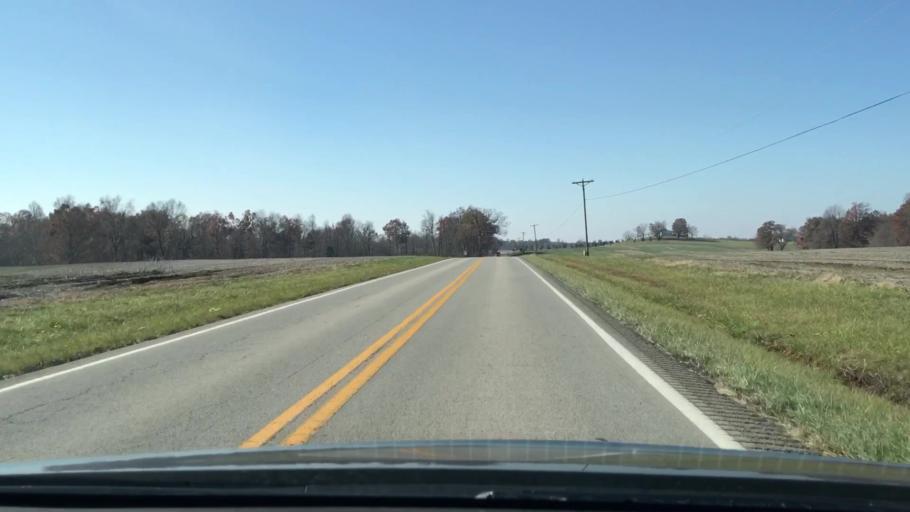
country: US
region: Kentucky
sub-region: Edmonson County
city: Brownsville
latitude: 37.3317
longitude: -86.2518
